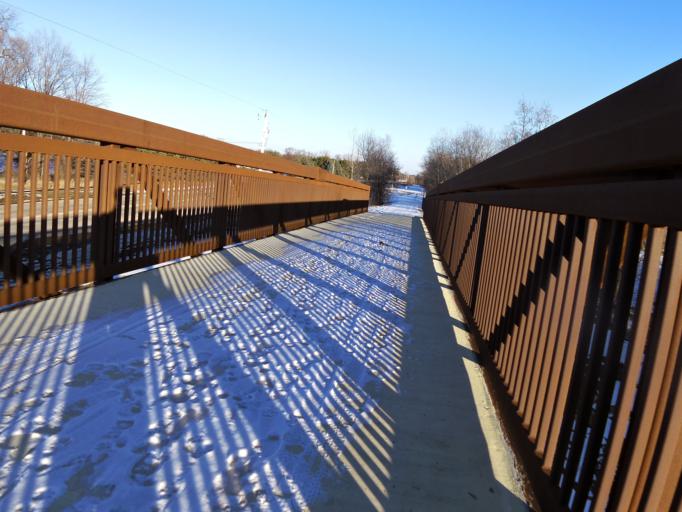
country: US
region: Minnesota
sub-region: Washington County
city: Grant
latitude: 45.0722
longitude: -92.8622
